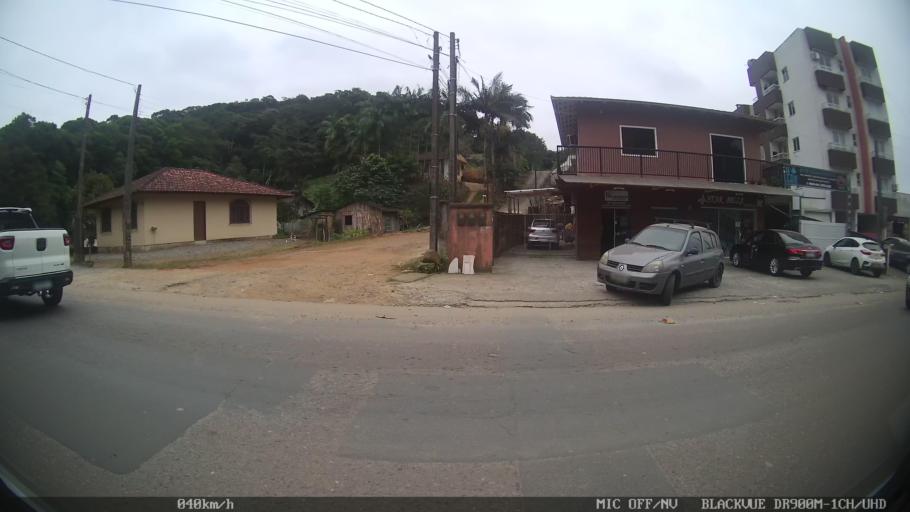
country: BR
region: Santa Catarina
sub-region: Joinville
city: Joinville
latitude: -26.3620
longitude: -48.8203
